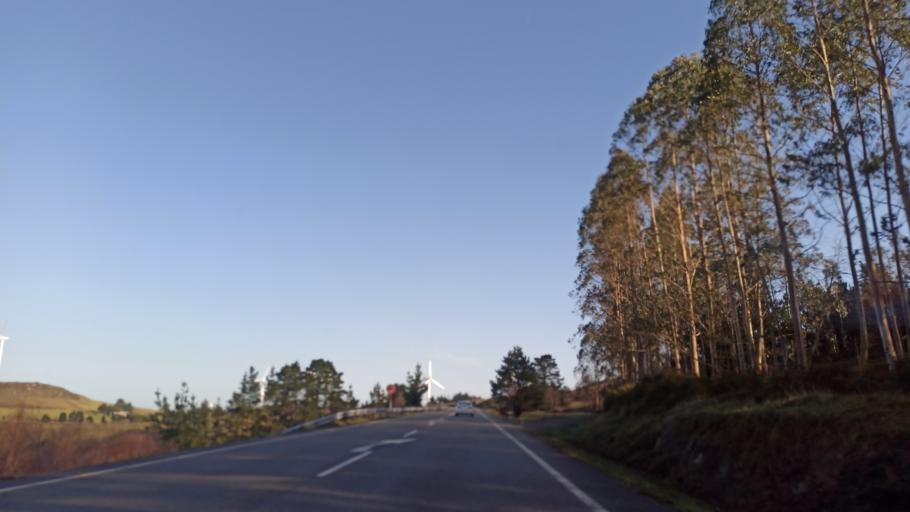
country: ES
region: Galicia
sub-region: Provincia da Coruna
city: As Pontes de Garcia Rodriguez
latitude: 43.5315
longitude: -7.8101
